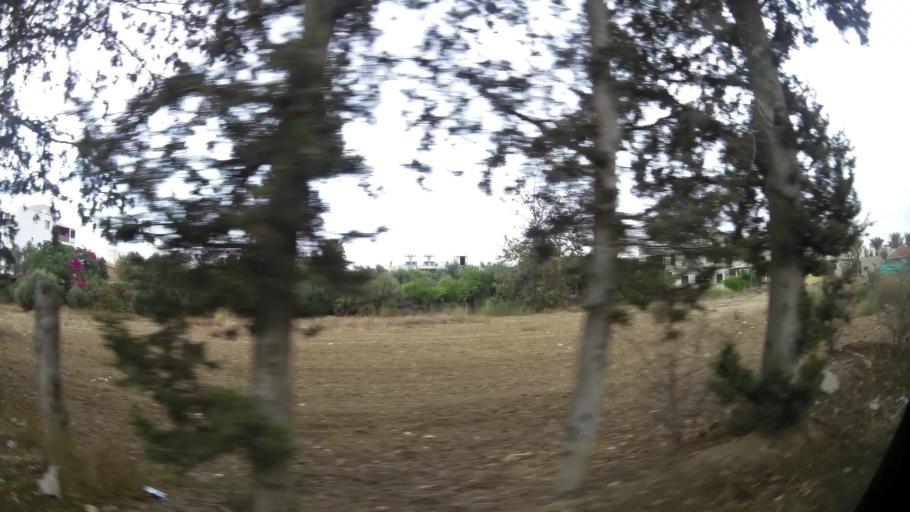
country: CY
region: Lefkosia
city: Geri
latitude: 35.0996
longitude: 33.3808
